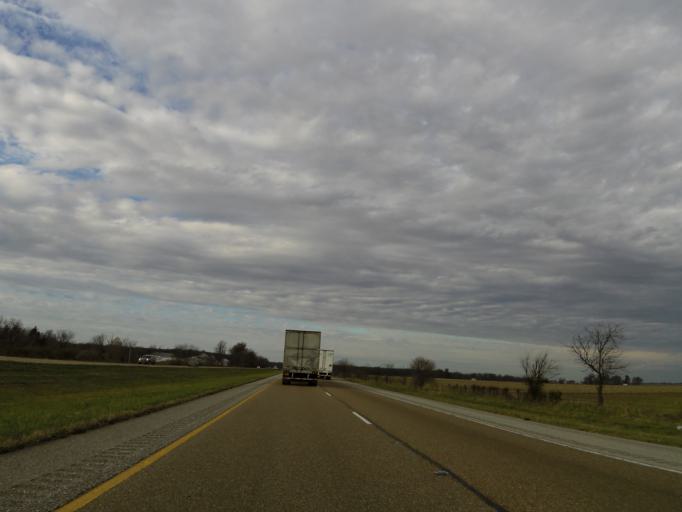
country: US
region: Illinois
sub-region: Washington County
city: Nashville
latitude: 38.3913
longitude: -89.2833
